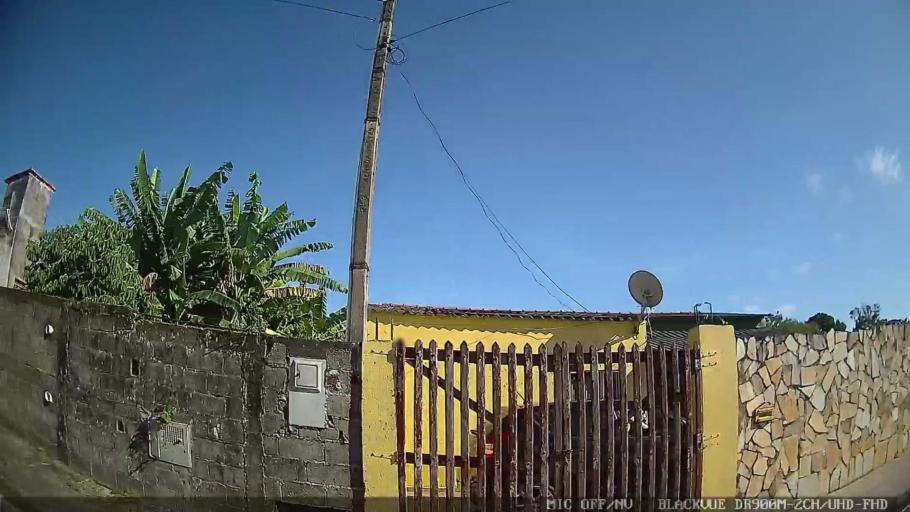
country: BR
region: Sao Paulo
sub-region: Peruibe
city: Peruibe
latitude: -24.2727
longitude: -46.9461
